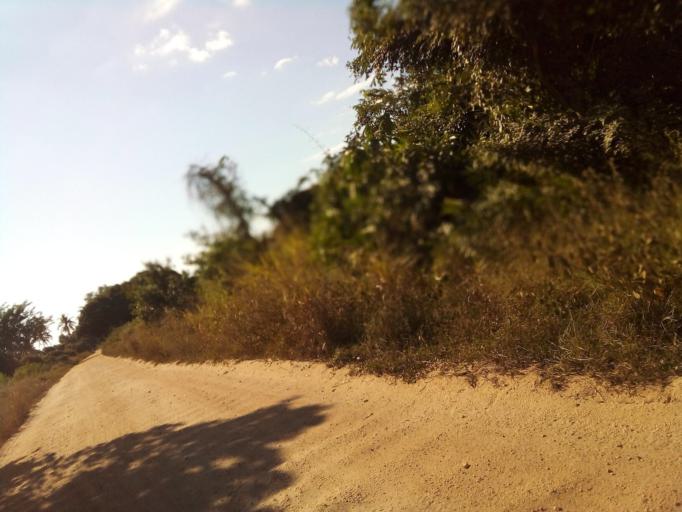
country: MZ
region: Zambezia
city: Quelimane
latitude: -17.5401
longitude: 36.6248
